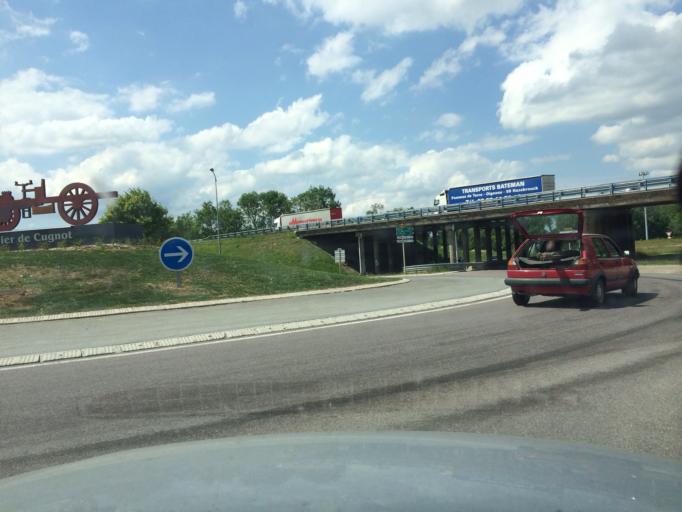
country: FR
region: Lorraine
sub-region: Departement de la Meuse
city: Vacon
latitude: 48.6908
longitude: 5.6228
